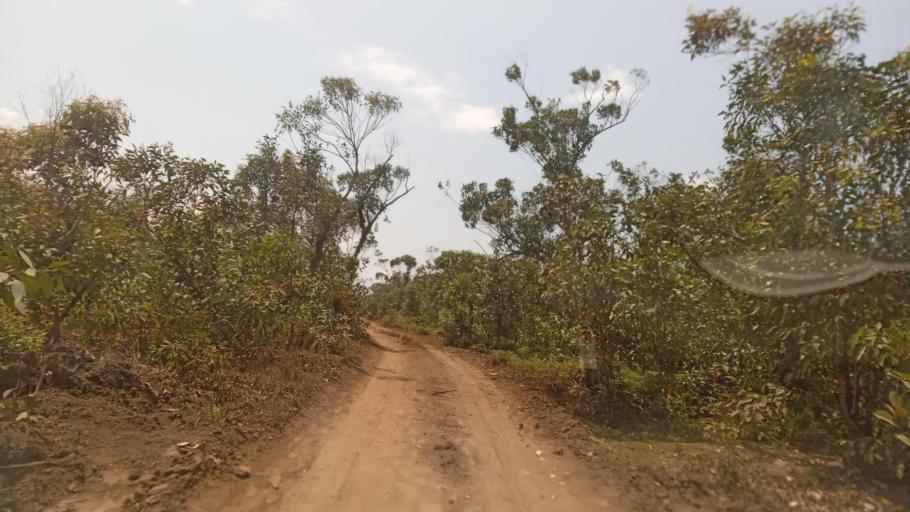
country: MG
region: Atsimo-Atsinanana
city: Vohipaho
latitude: -23.6196
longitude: 47.6039
